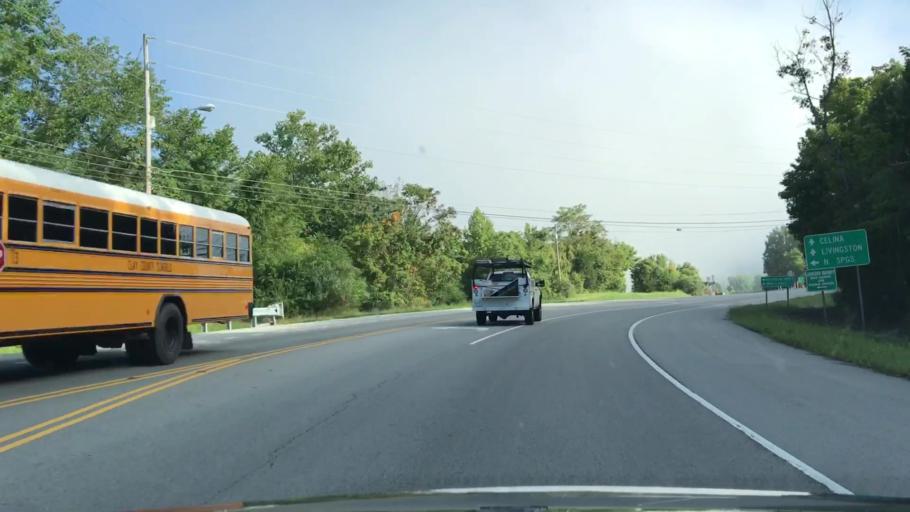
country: US
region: Tennessee
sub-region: Jackson County
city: Gainesboro
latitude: 36.3710
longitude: -85.6527
